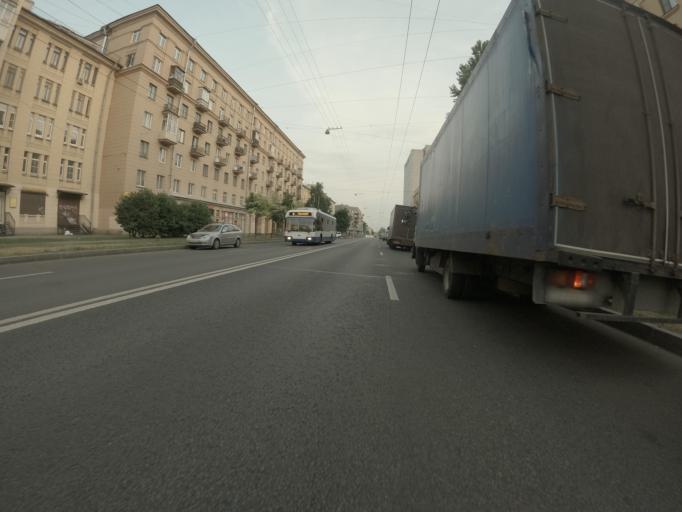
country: RU
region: Leningrad
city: Kalininskiy
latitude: 59.9729
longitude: 30.3887
